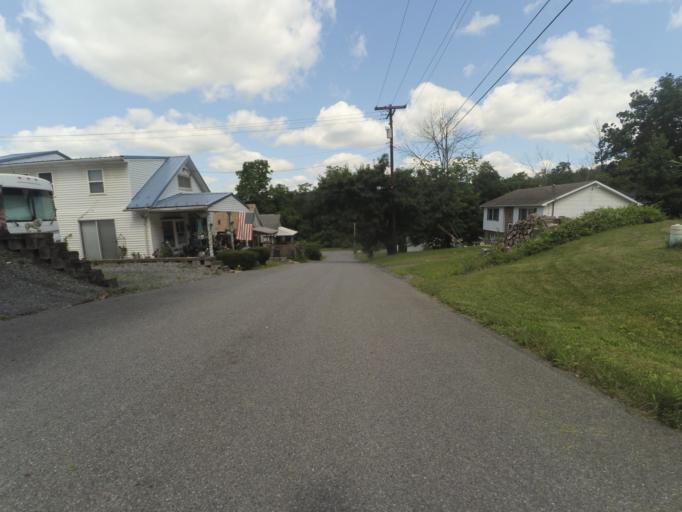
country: US
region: Pennsylvania
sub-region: Centre County
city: Stormstown
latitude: 40.8000
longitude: -78.0457
